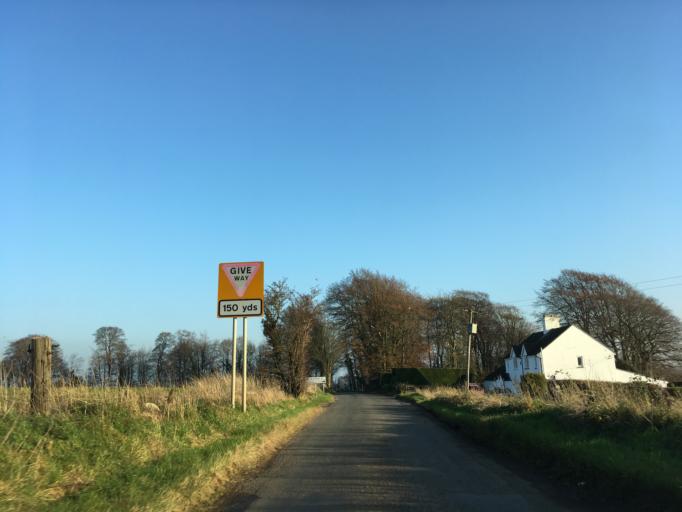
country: GB
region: England
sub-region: South Gloucestershire
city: Horton
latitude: 51.5553
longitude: -2.3254
